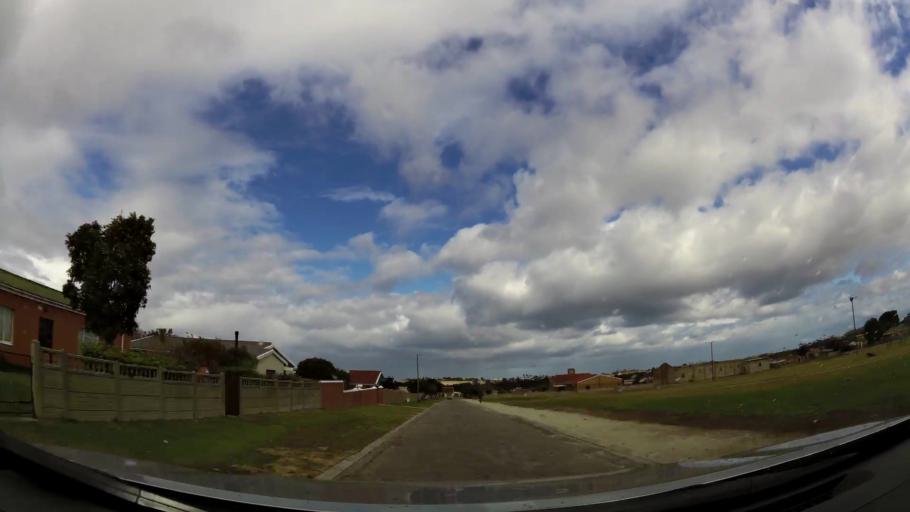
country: ZA
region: Western Cape
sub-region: Eden District Municipality
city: George
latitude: -34.0201
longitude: 22.4674
